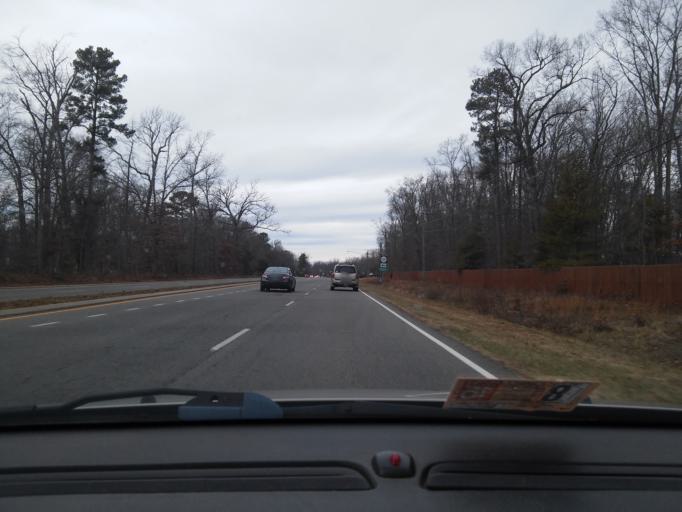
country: US
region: Virginia
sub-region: Chesterfield County
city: Bon Air
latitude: 37.5384
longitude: -77.6393
